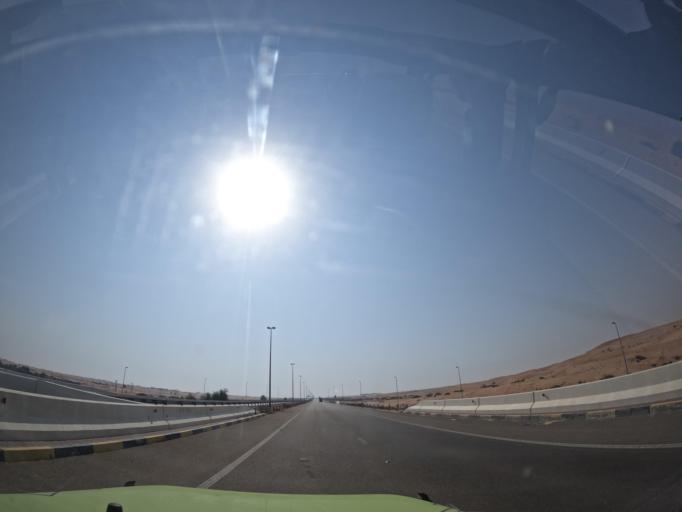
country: OM
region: Al Buraimi
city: Al Buraymi
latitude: 24.5113
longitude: 55.5664
